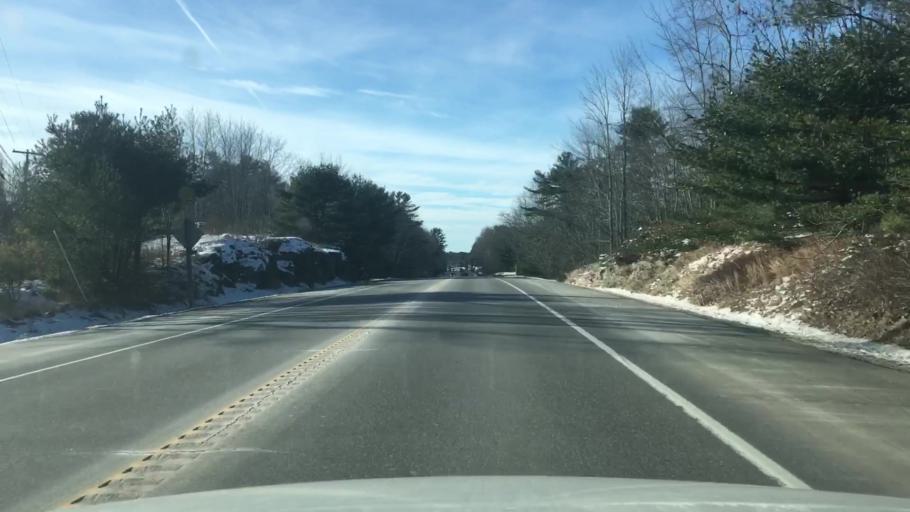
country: US
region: Maine
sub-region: Sagadahoc County
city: Woolwich
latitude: 43.9408
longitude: -69.7650
